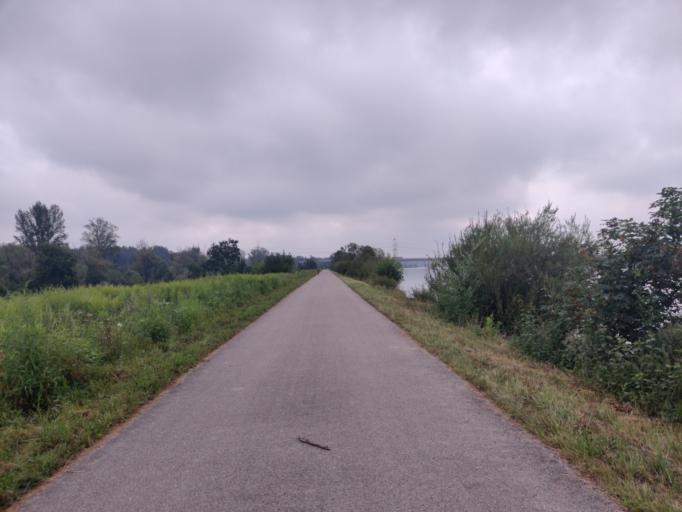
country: AT
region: Lower Austria
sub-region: Politischer Bezirk Krems
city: Grafenegg
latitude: 48.3895
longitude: 15.7125
